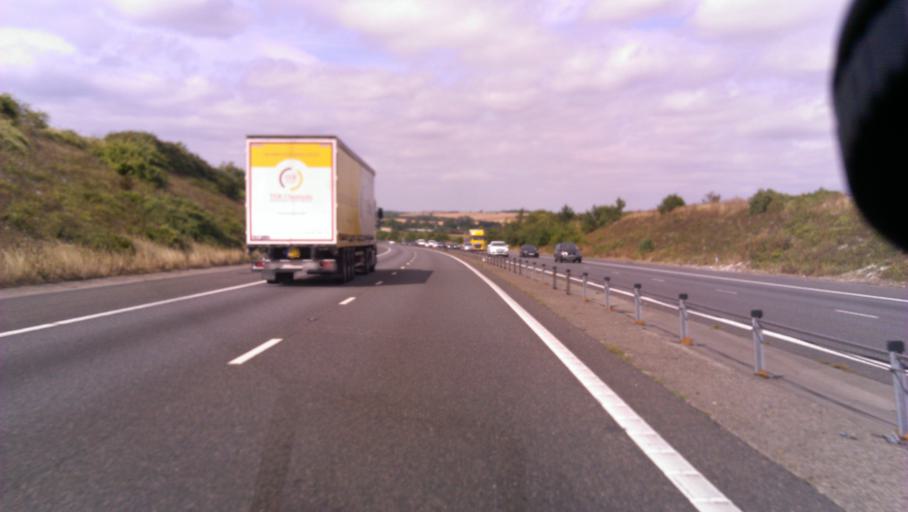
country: GB
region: England
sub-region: Essex
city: Saffron Walden
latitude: 52.0462
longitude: 0.1918
